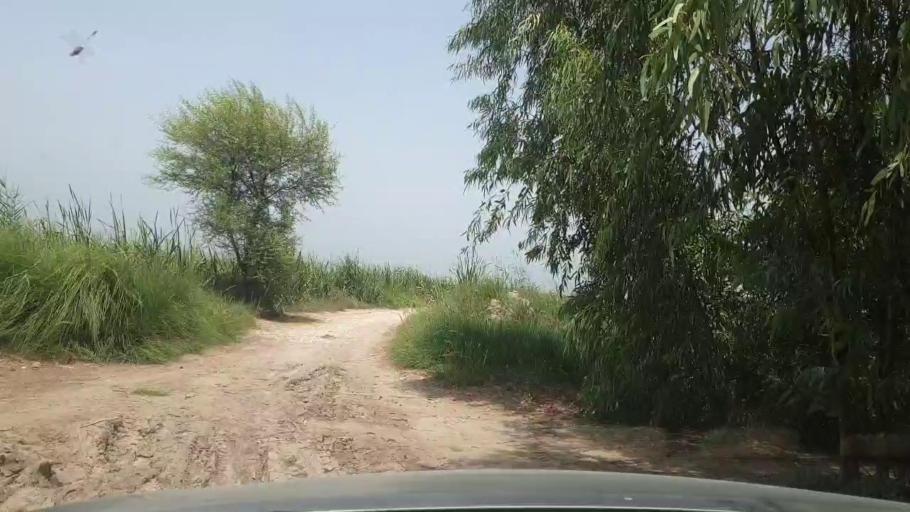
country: PK
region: Sindh
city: Garhi Yasin
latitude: 27.9467
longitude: 68.4293
